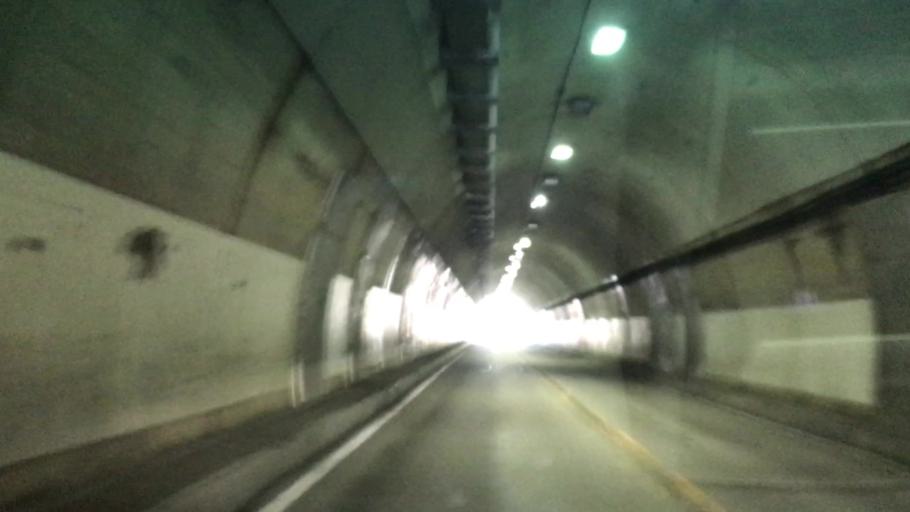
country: JP
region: Hokkaido
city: Iwanai
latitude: 43.1088
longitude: 140.4517
